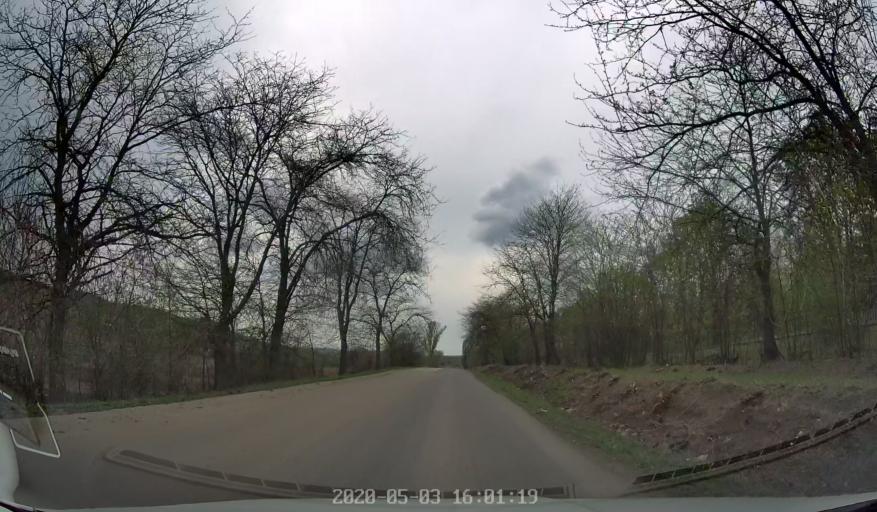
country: MD
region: Stinga Nistrului
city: Bucovat
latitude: 47.1654
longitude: 28.4104
